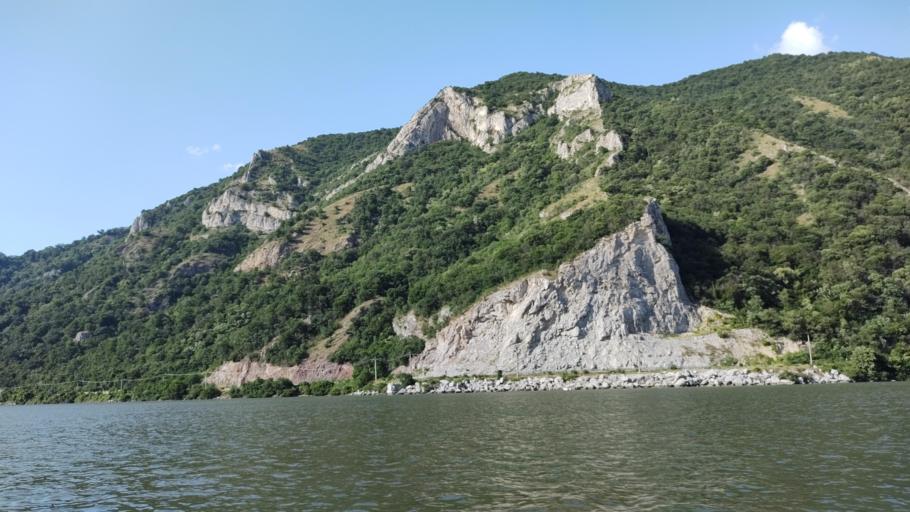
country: RO
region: Caras-Severin
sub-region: Comuna Berzasca
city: Berzasca
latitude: 44.5996
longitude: 22.0172
